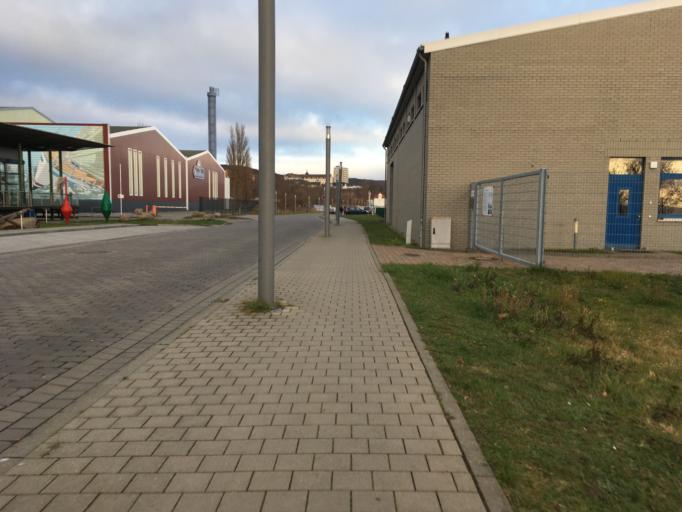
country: DE
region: Mecklenburg-Vorpommern
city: Sassnitz
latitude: 54.5084
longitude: 13.6328
